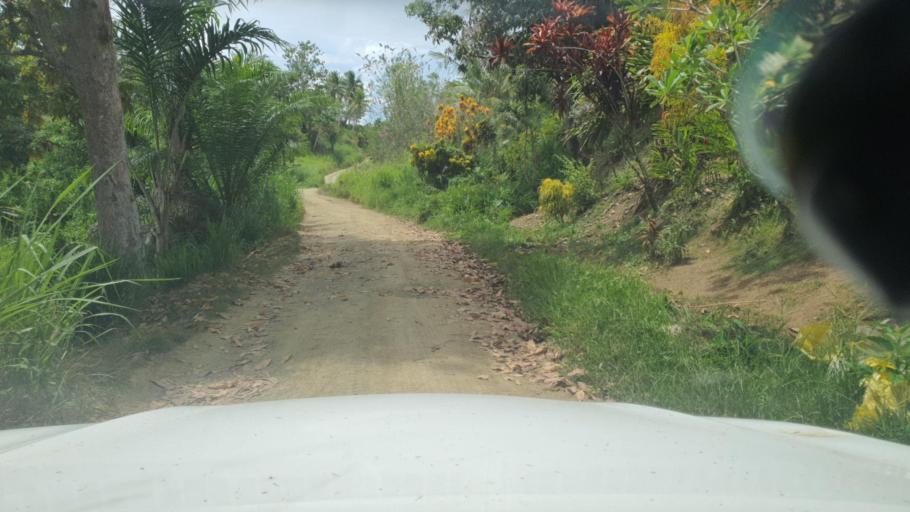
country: SB
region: Guadalcanal
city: Honiara
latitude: -9.4845
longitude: 160.3373
